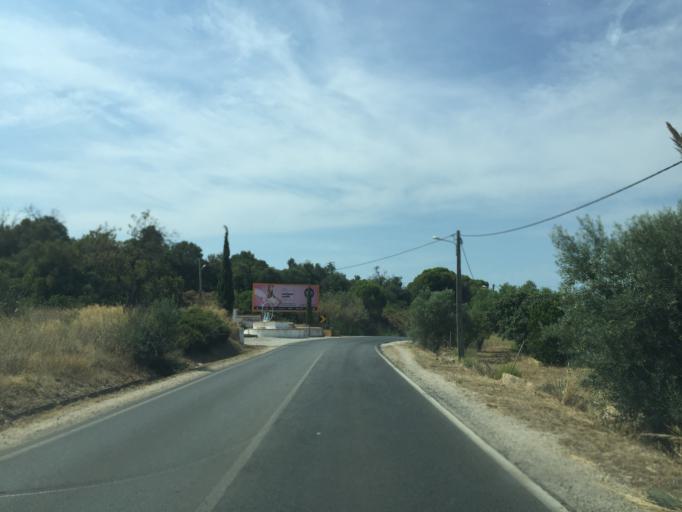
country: PT
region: Faro
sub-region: Loule
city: Almancil
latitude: 37.0754
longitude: -8.0647
